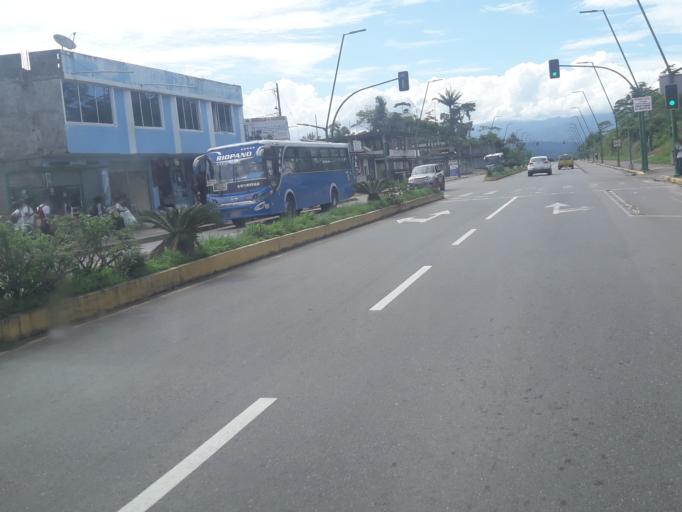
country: EC
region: Napo
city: Tena
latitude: -1.0186
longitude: -77.8067
